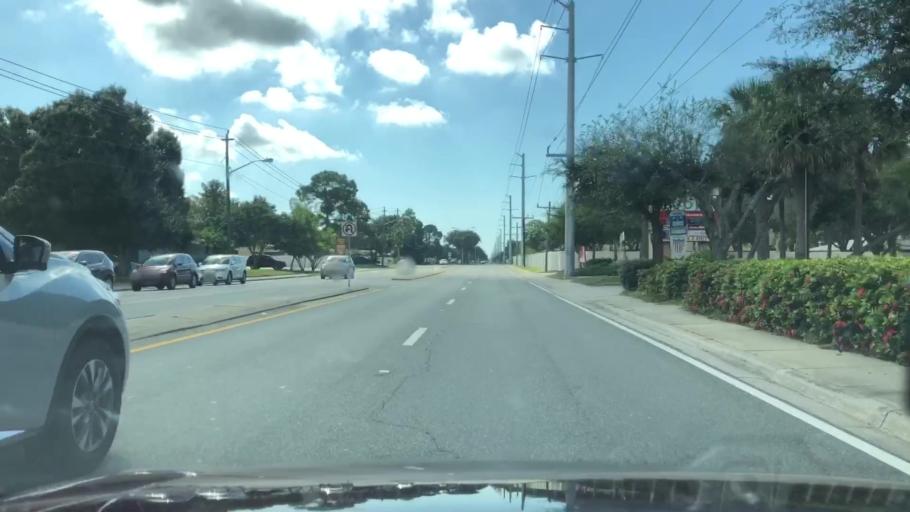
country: US
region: Florida
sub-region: Sarasota County
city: South Gate Ridge
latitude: 27.2686
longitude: -82.4976
